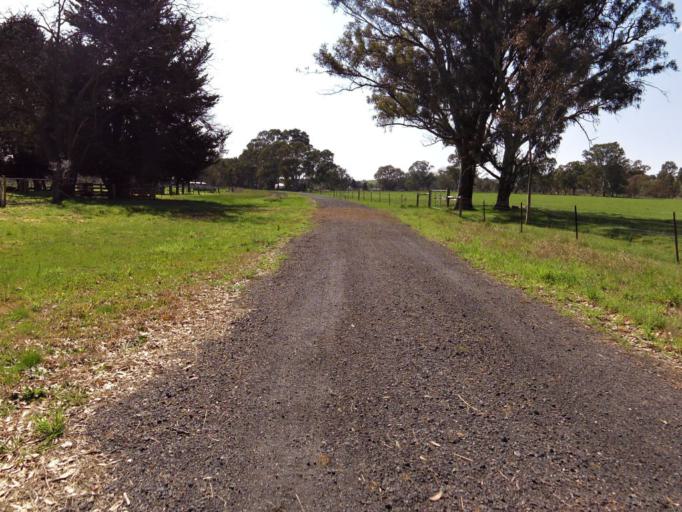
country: AU
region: Victoria
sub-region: Murrindindi
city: Alexandra
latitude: -37.1106
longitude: 145.6112
